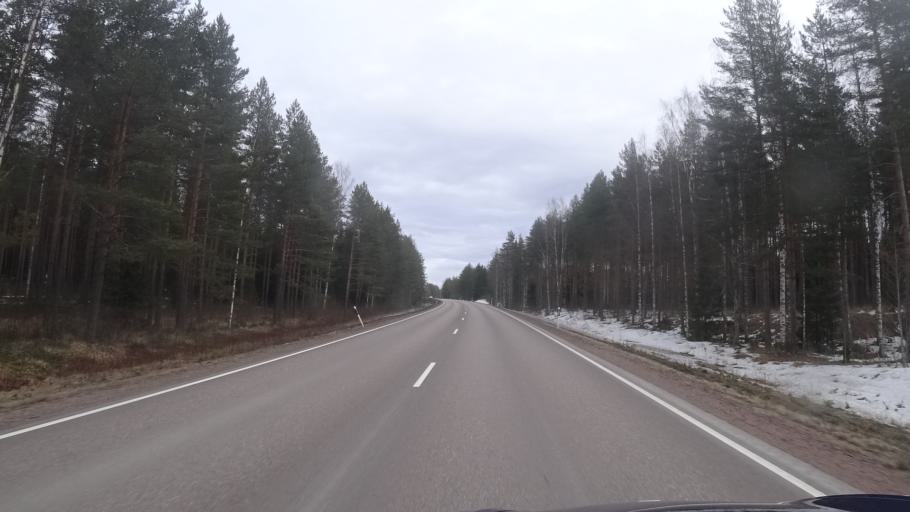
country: FI
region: Kymenlaakso
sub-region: Kouvola
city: Anjala
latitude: 60.6929
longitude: 26.6725
